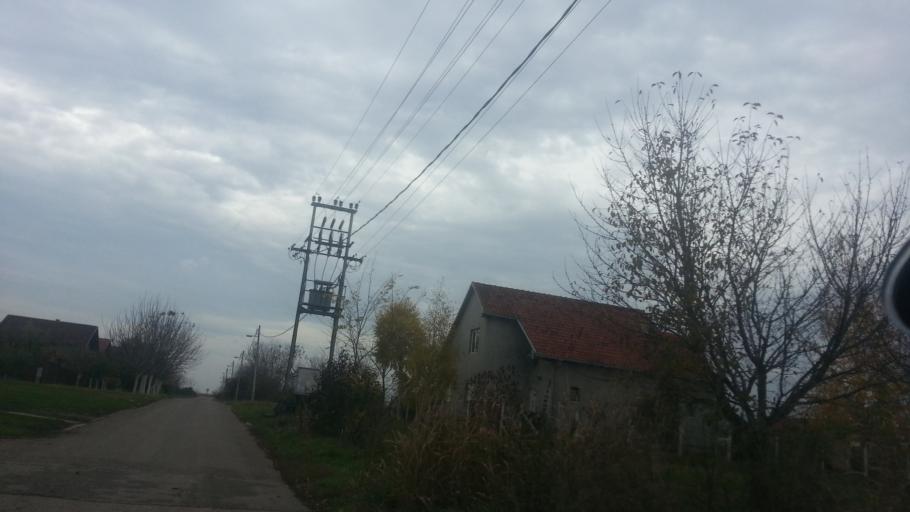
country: RS
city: Golubinci
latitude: 44.9837
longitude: 20.0489
